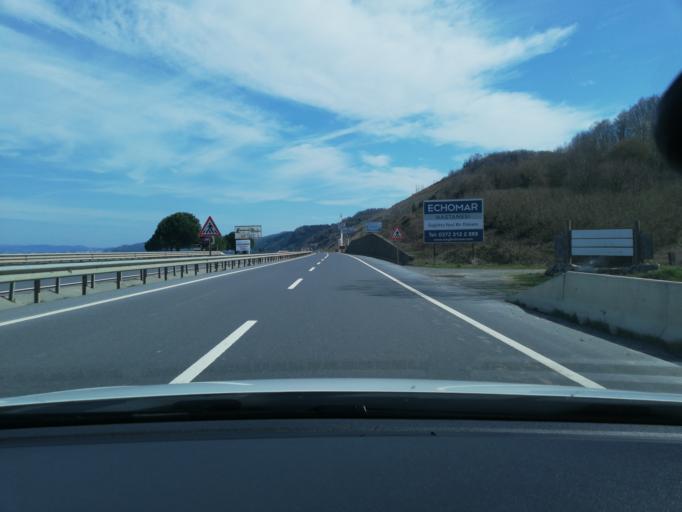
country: TR
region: Zonguldak
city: Alapli
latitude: 41.1111
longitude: 31.2786
